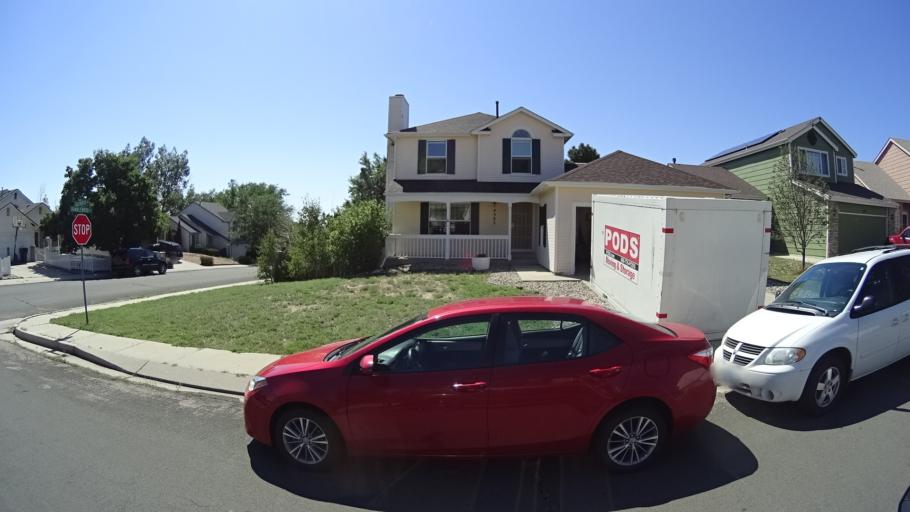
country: US
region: Colorado
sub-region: El Paso County
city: Black Forest
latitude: 38.9429
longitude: -104.7445
